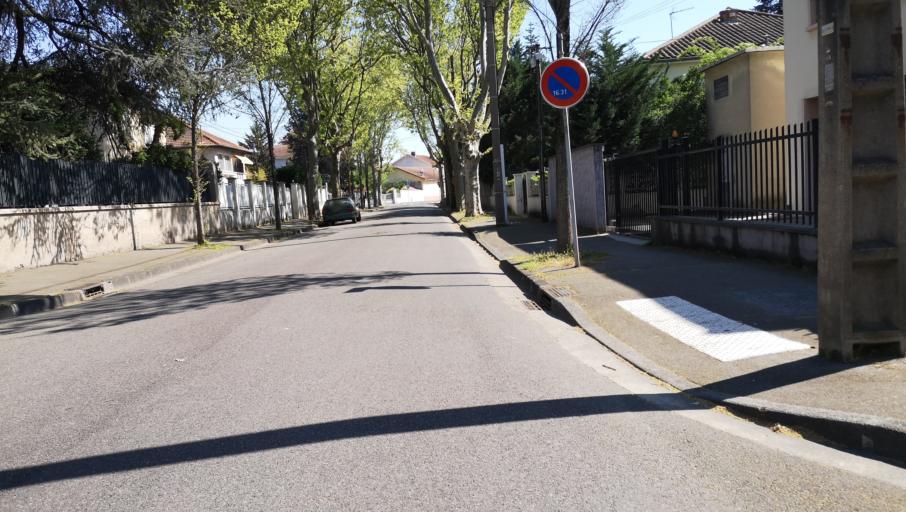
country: FR
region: Rhone-Alpes
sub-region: Departement du Rhone
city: Bron
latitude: 45.7353
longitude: 4.9120
